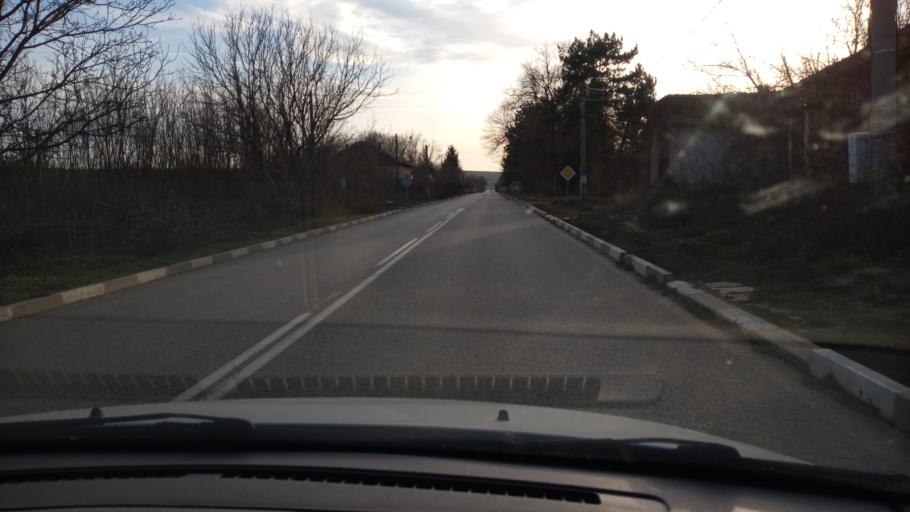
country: BG
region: Pleven
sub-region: Obshtina Pleven
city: Slavyanovo
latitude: 43.5556
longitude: 24.8662
